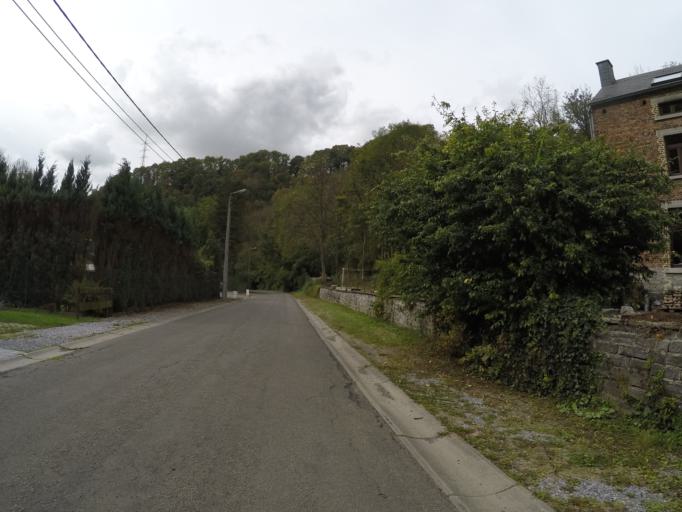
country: BE
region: Wallonia
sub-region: Province de Namur
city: Dinant
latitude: 50.2748
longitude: 4.9320
